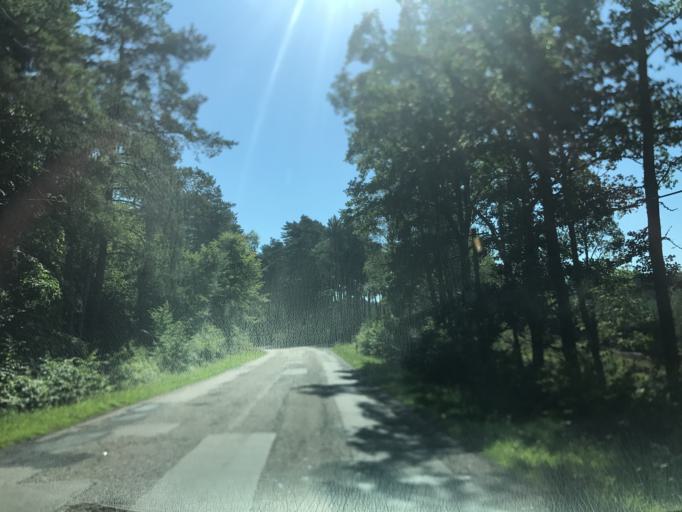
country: PL
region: Pomeranian Voivodeship
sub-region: Powiat bytowski
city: Czarna Dabrowka
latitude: 54.3411
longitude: 17.6109
